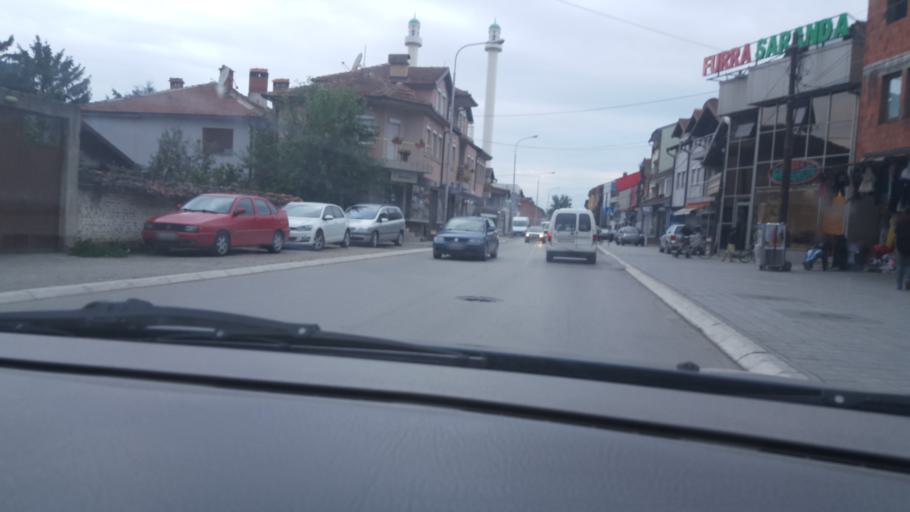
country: XK
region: Gjakova
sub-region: Komuna e Gjakoves
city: Gjakove
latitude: 42.3900
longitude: 20.4262
